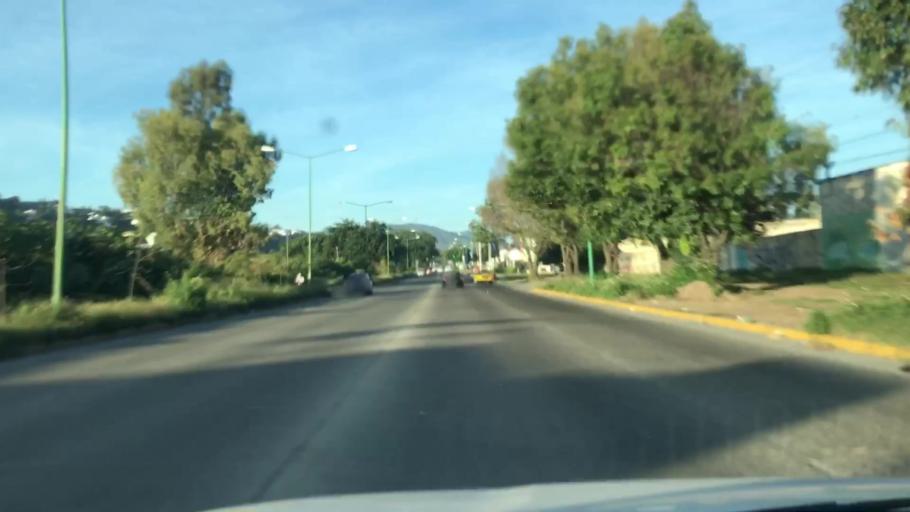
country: MX
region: Jalisco
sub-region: Tlajomulco de Zuniga
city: Palomar
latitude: 20.6281
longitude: -103.4582
